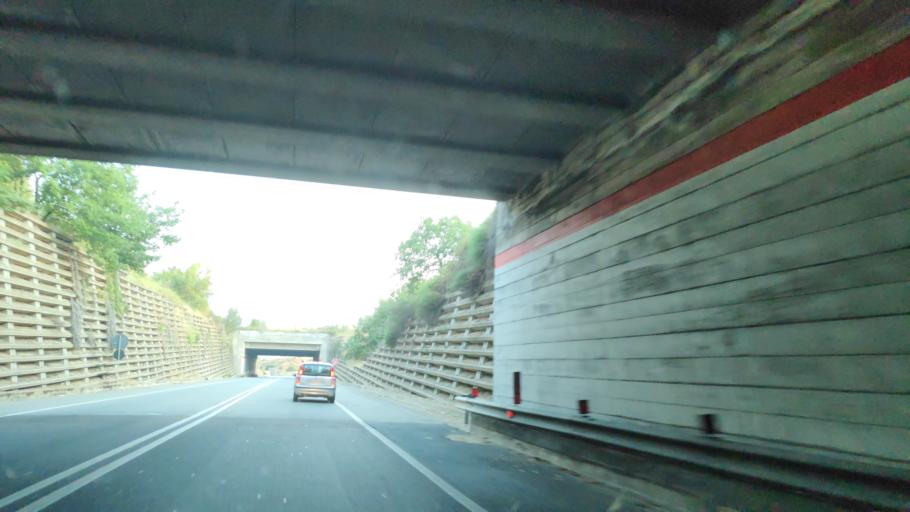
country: IT
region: Calabria
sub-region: Provincia di Catanzaro
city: Soverato Superiore
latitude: 38.6951
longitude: 16.5386
